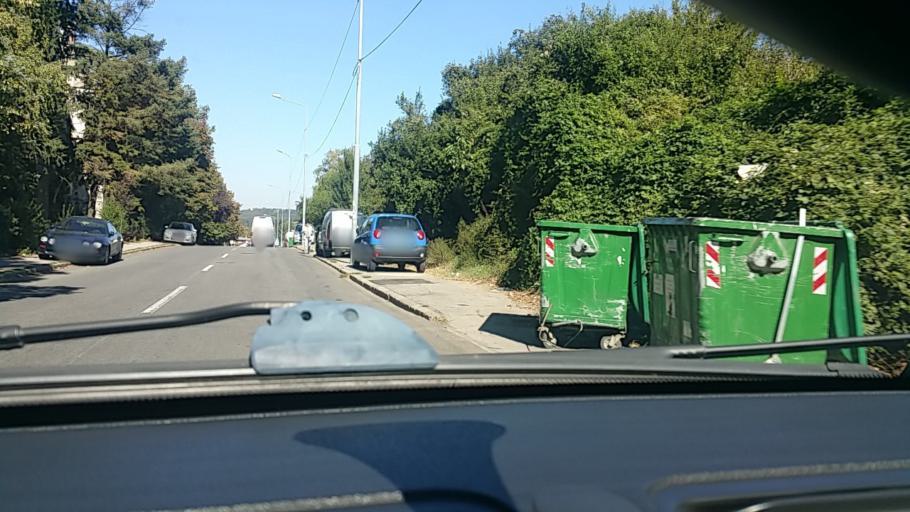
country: RS
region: Central Serbia
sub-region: Belgrade
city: Rakovica
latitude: 44.7467
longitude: 20.4615
